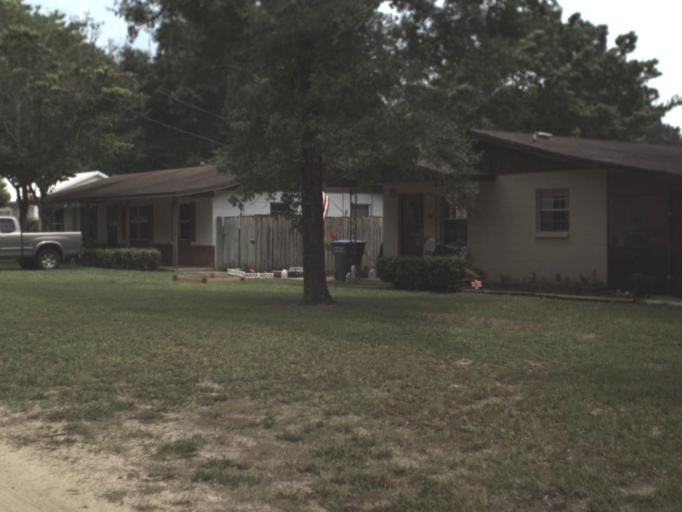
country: US
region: Florida
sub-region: Levy County
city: Chiefland
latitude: 29.4965
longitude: -82.8666
